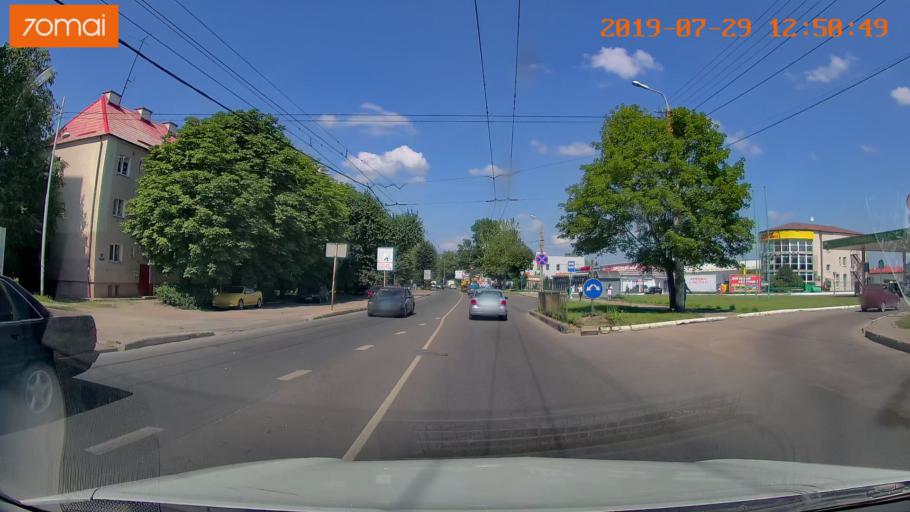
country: RU
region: Kaliningrad
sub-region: Gorod Kaliningrad
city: Kaliningrad
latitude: 54.6894
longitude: 20.5317
